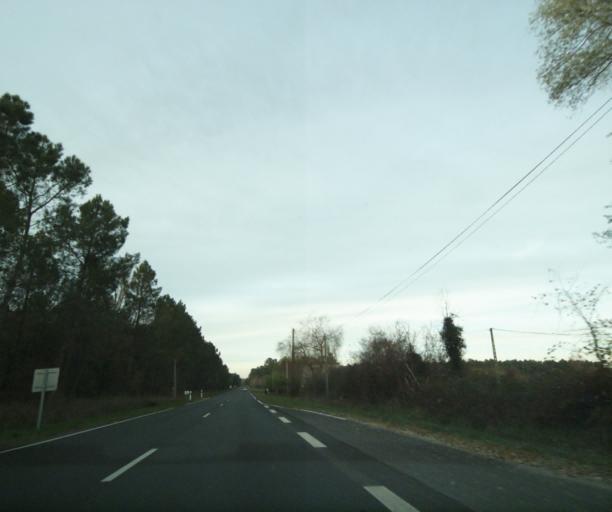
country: FR
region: Aquitaine
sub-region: Departement de la Gironde
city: Bazas
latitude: 44.3457
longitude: -0.2358
